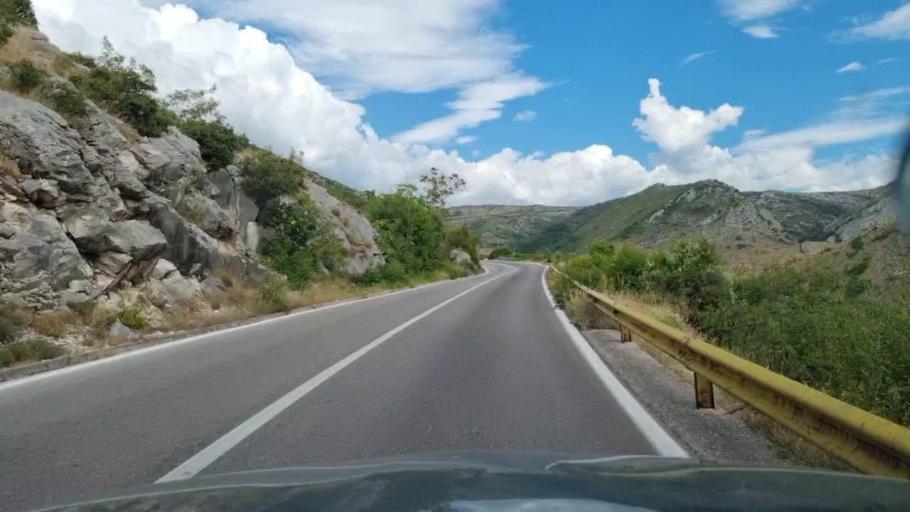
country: BA
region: Federation of Bosnia and Herzegovina
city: Blagaj
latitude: 43.2642
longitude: 17.9032
